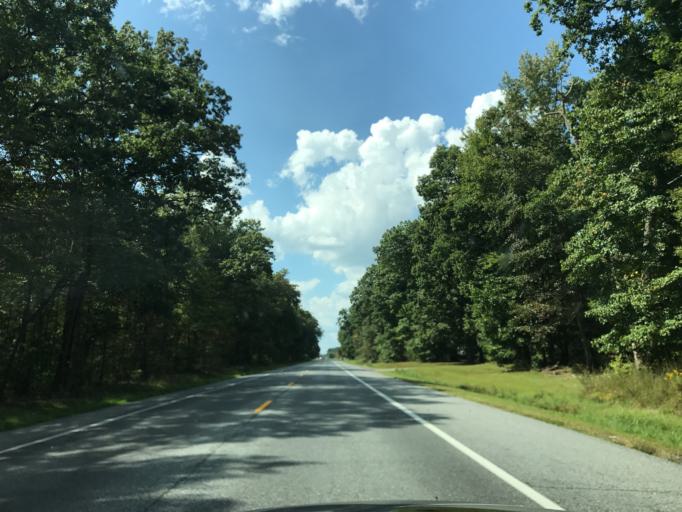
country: US
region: Delaware
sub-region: Kent County
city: Clayton
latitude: 39.1956
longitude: -75.7986
